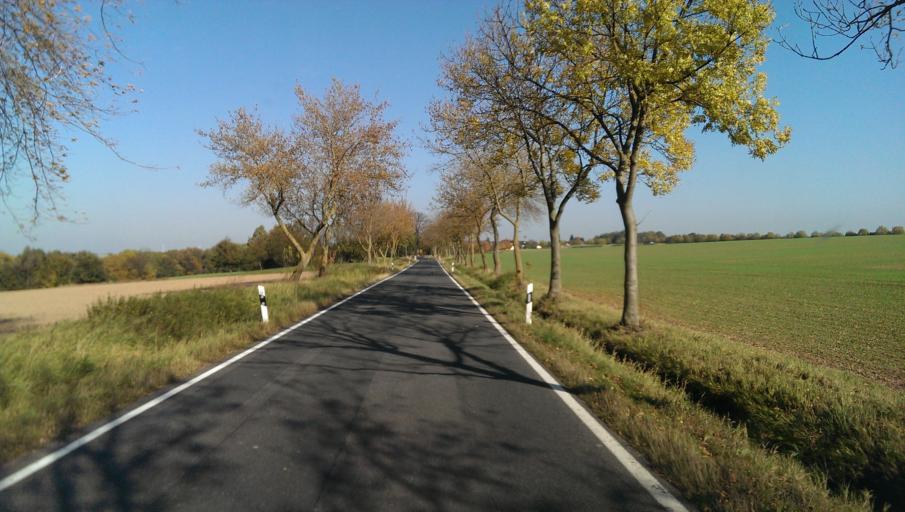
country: DE
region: Saxony
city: Waldheim
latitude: 51.0958
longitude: 13.0500
